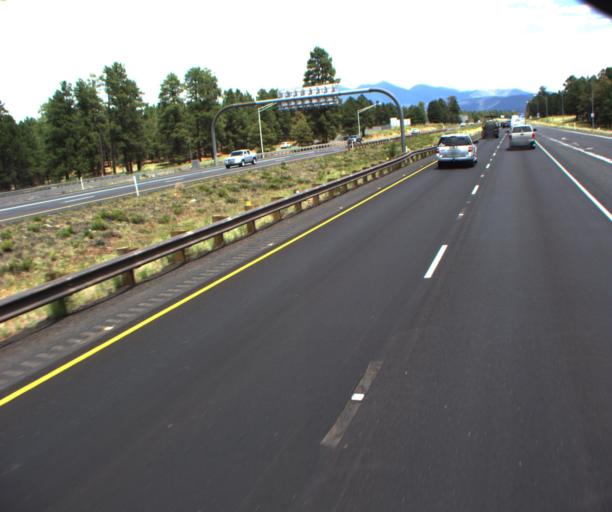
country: US
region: Arizona
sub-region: Coconino County
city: Kachina Village
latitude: 35.1452
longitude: -111.6833
